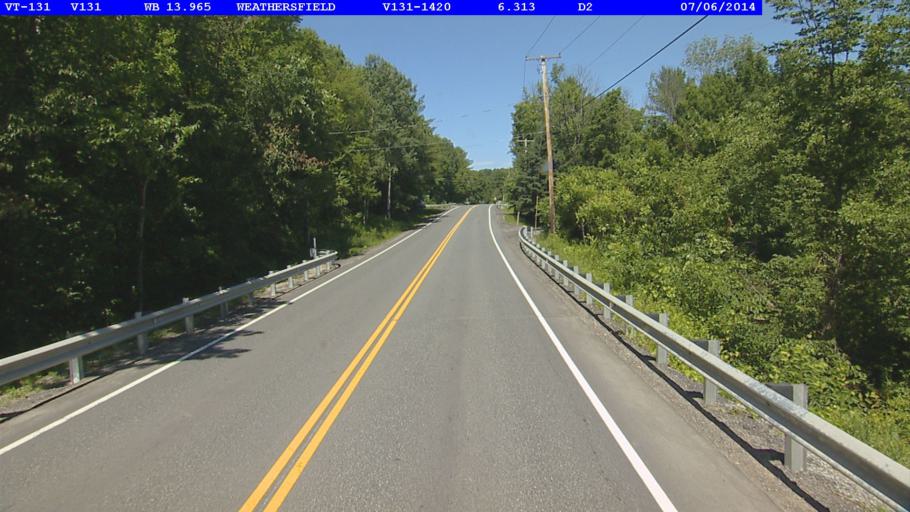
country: US
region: Vermont
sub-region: Windsor County
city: Windsor
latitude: 43.4107
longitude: -72.4476
